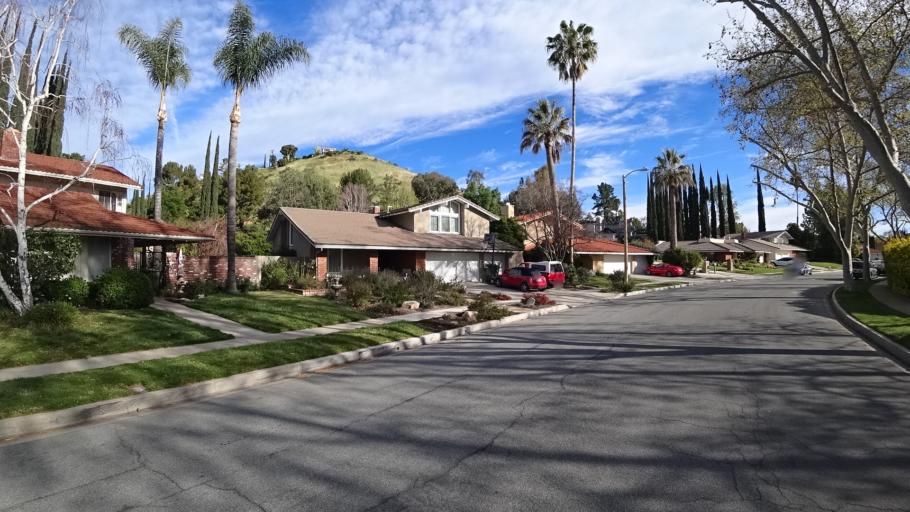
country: US
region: California
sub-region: Ventura County
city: Thousand Oaks
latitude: 34.1487
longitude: -118.8434
